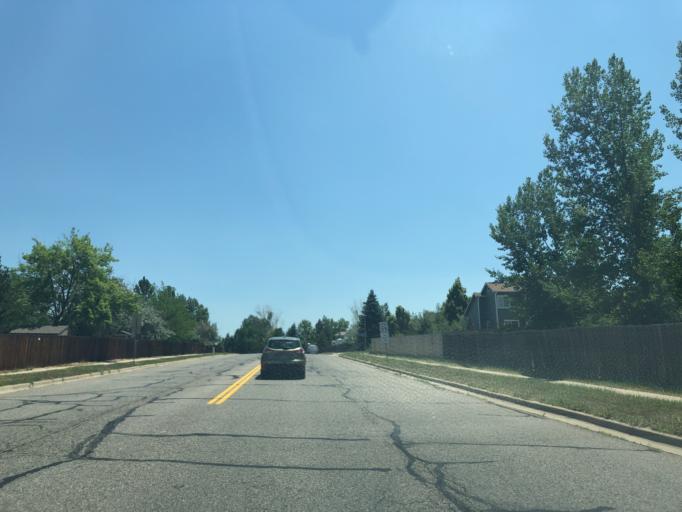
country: US
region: Colorado
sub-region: Arapahoe County
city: Dove Valley
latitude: 39.6269
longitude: -104.7602
